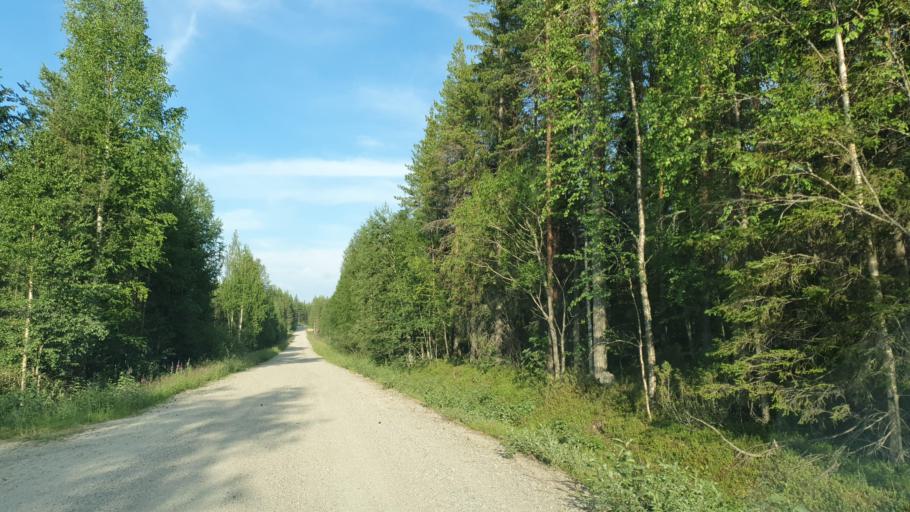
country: FI
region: Kainuu
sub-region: Kehys-Kainuu
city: Kuhmo
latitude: 64.2850
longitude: 29.7585
